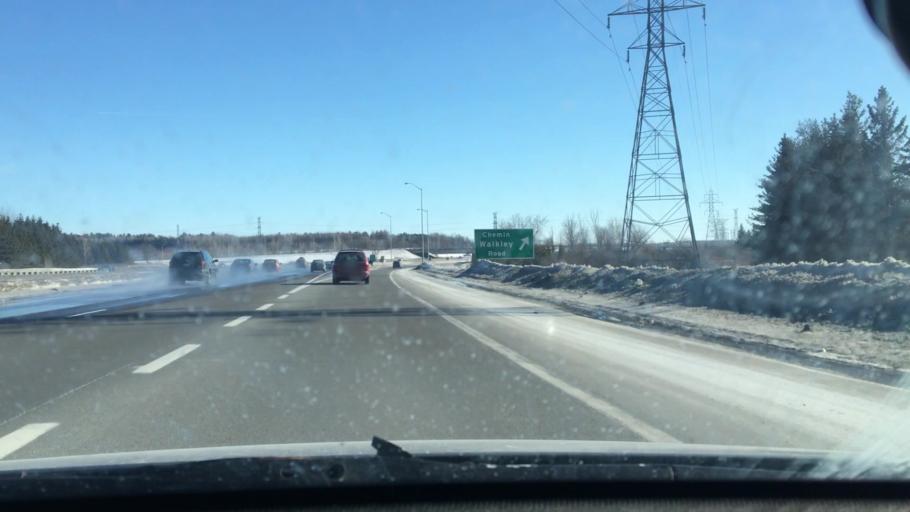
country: CA
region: Ontario
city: Ottawa
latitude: 45.4032
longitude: -75.5959
